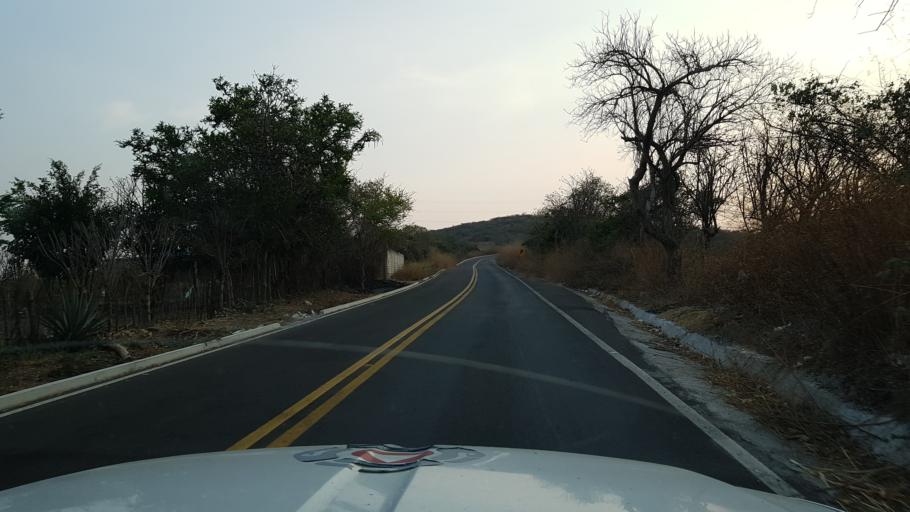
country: MX
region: Morelos
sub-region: Ayala
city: Olintepec
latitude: 18.7350
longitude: -99.0107
